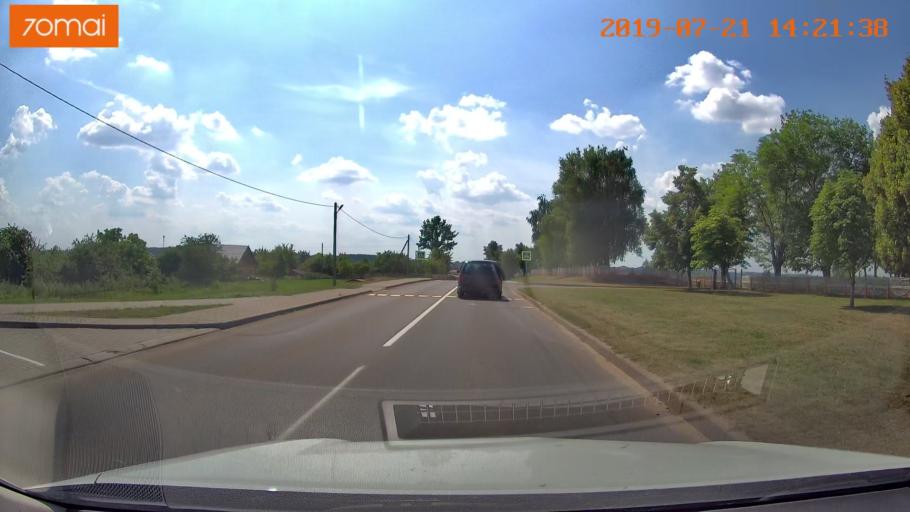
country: BY
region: Grodnenskaya
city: Karelichy
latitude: 53.5756
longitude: 26.1432
